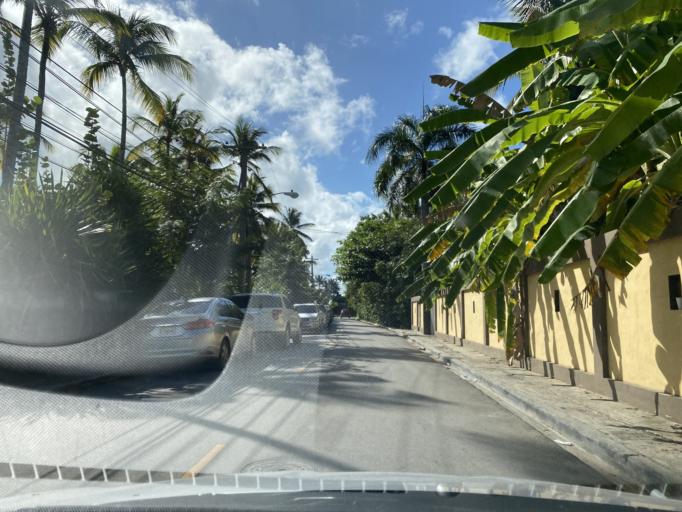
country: DO
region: Samana
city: Las Terrenas
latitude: 19.3129
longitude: -69.5644
